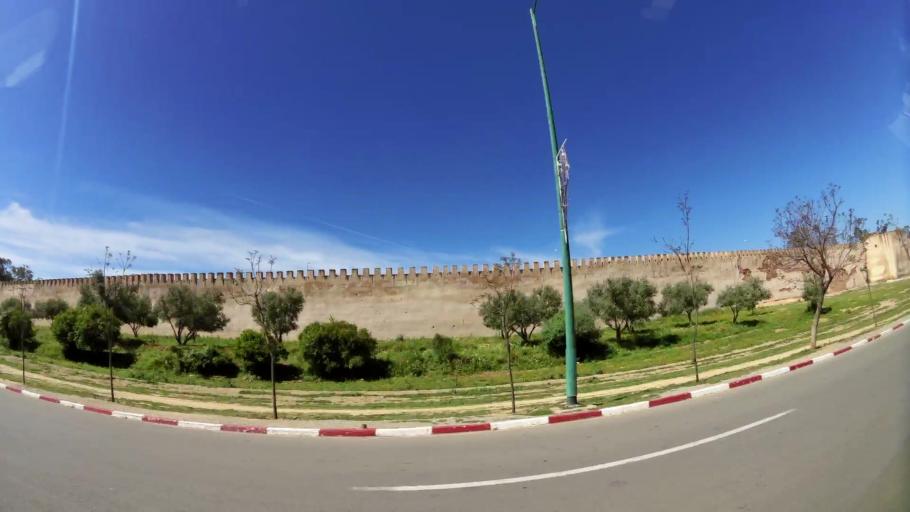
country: MA
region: Meknes-Tafilalet
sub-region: Meknes
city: Meknes
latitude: 33.8780
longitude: -5.5393
